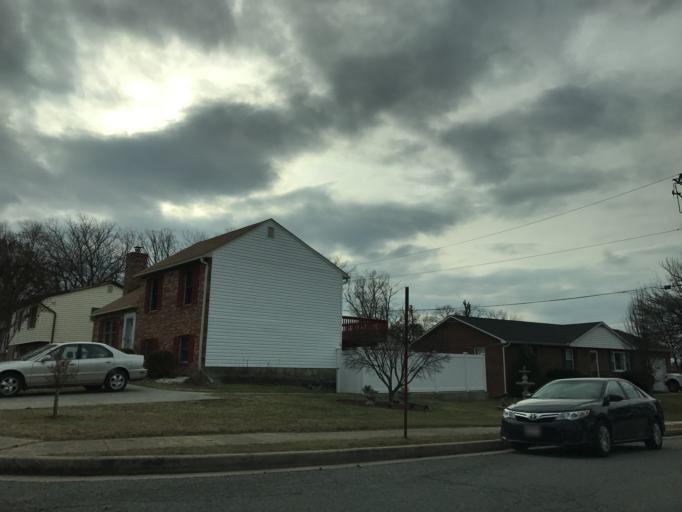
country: US
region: Maryland
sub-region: Baltimore County
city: Essex
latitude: 39.3251
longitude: -76.4670
